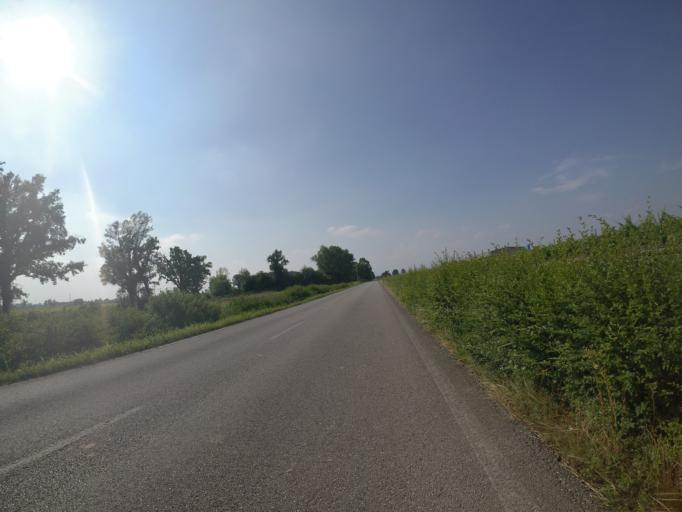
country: IT
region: Friuli Venezia Giulia
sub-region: Provincia di Udine
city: Camino al Tagliamento
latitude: 45.9257
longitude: 12.9628
